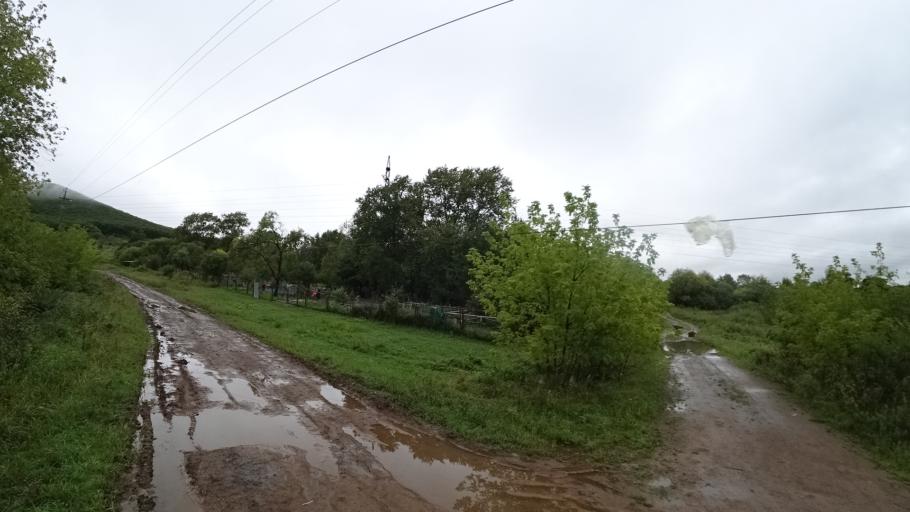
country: RU
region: Primorskiy
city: Monastyrishche
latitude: 44.2634
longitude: 132.4257
